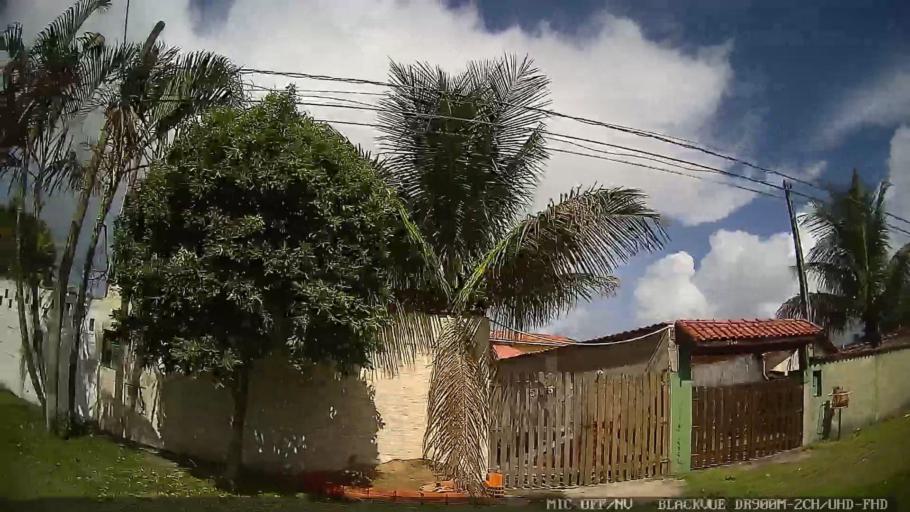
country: BR
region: Sao Paulo
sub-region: Itanhaem
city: Itanhaem
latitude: -24.2380
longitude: -46.8880
